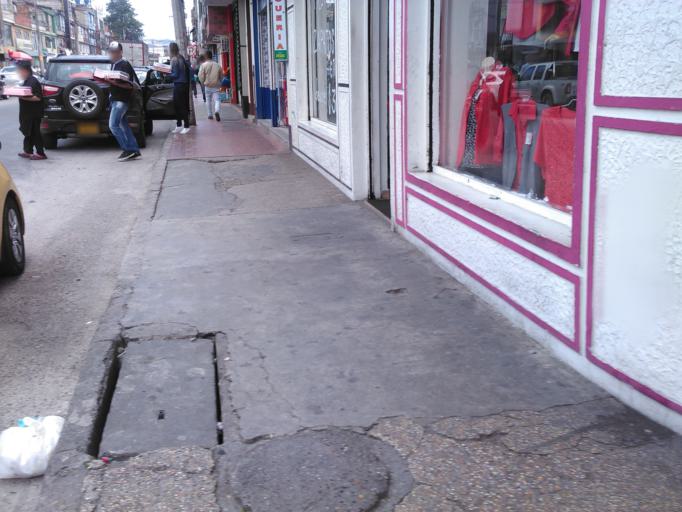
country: CO
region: Bogota D.C.
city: Bogota
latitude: 4.6216
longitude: -74.1180
